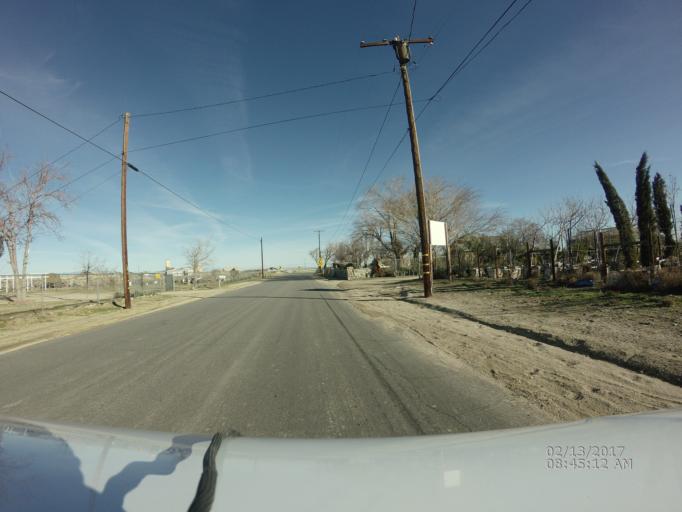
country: US
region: California
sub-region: Los Angeles County
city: Littlerock
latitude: 34.5406
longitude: -117.9882
